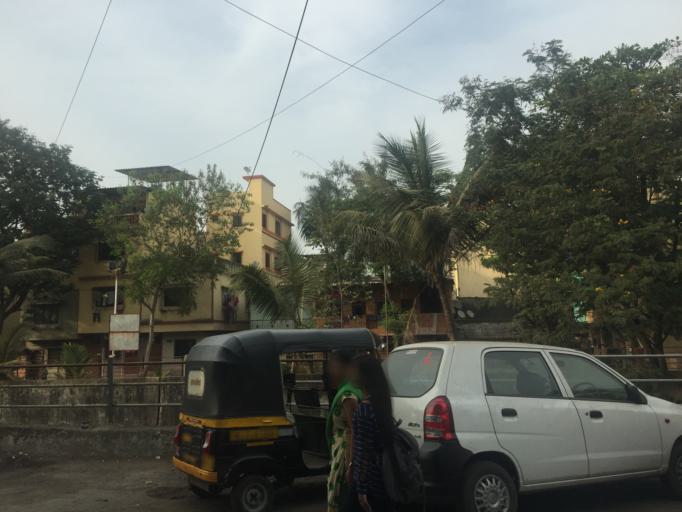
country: IN
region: Maharashtra
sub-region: Thane
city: Airoli
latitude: 19.1556
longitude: 72.9961
